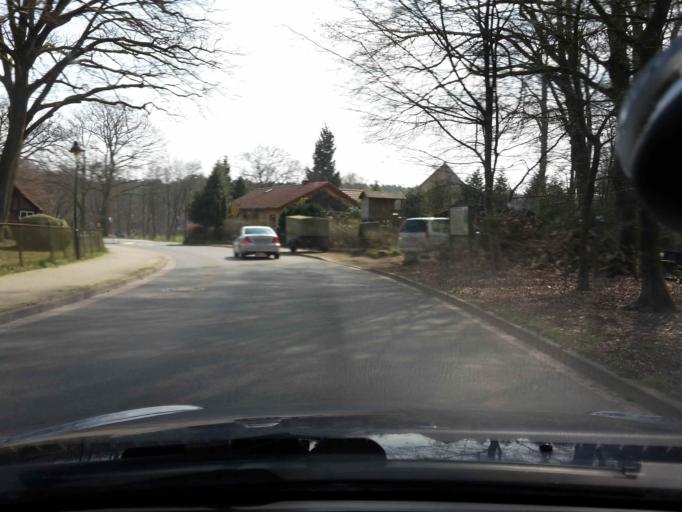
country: DE
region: Lower Saxony
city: Jesteburg
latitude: 53.2894
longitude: 9.9138
